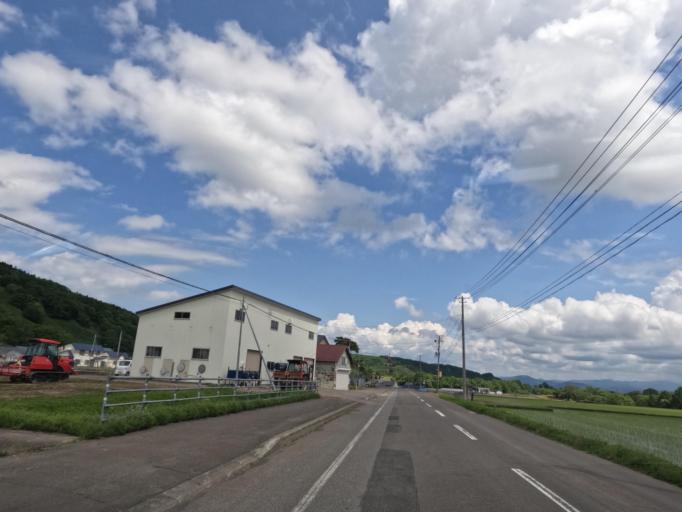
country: JP
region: Hokkaido
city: Takikawa
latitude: 43.5829
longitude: 141.8091
